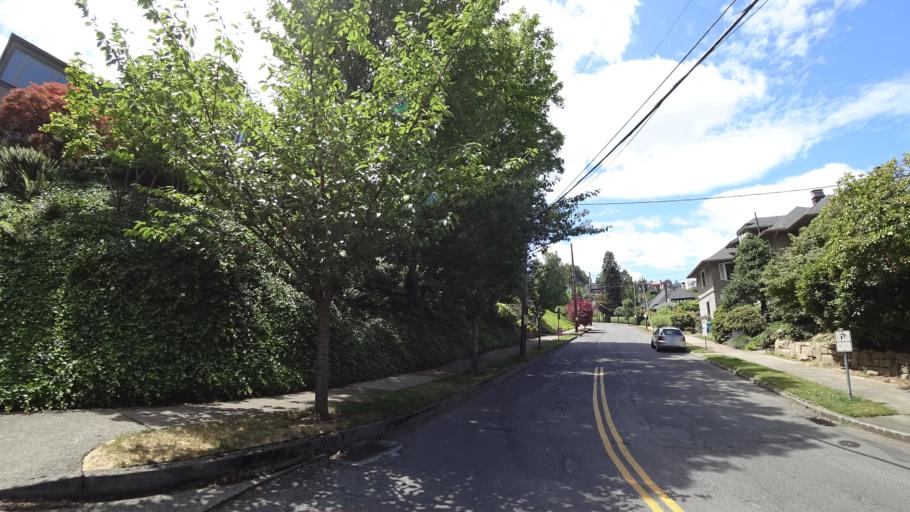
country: US
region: Oregon
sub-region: Multnomah County
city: Portland
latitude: 45.5282
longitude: -122.7038
